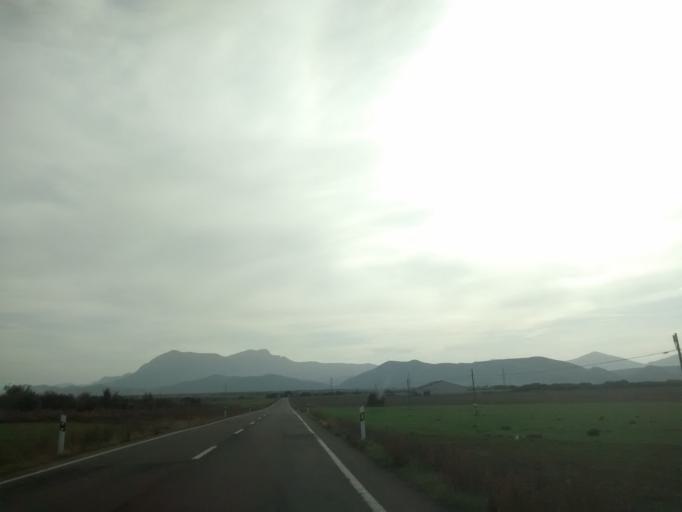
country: ES
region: Aragon
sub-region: Provincia de Huesca
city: Bailo
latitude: 42.5947
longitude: -0.8464
